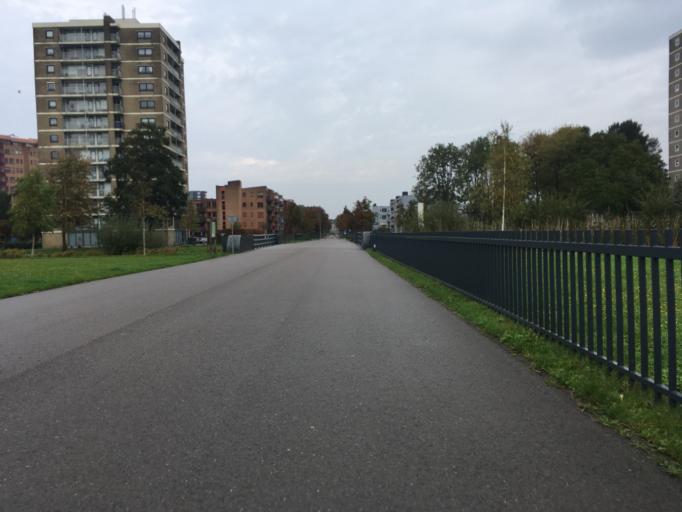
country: NL
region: North Holland
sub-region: Gemeente Haarlem
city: Haarlem
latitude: 52.3737
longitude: 4.6607
